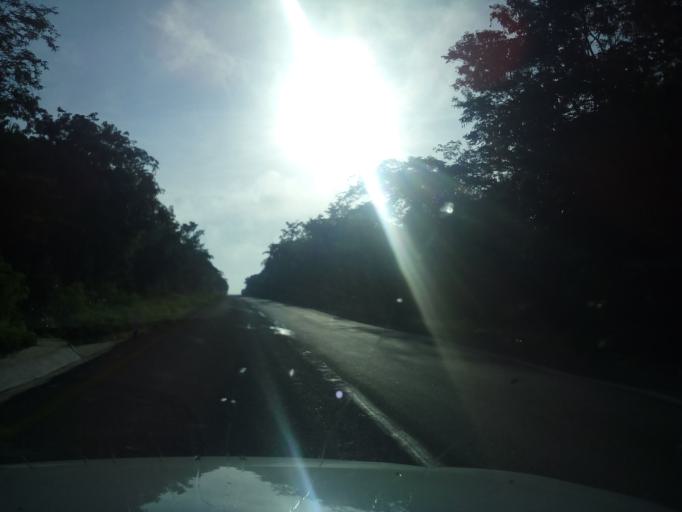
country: MX
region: Yucatan
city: Piste
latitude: 20.7471
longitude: -88.7034
